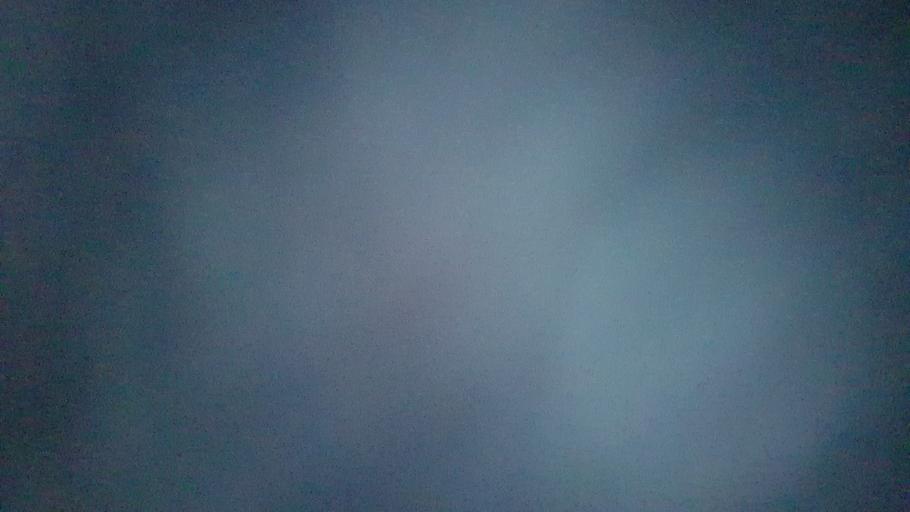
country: IT
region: Apulia
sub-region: Provincia di Lecce
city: Otranto
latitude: 40.1458
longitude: 18.4919
